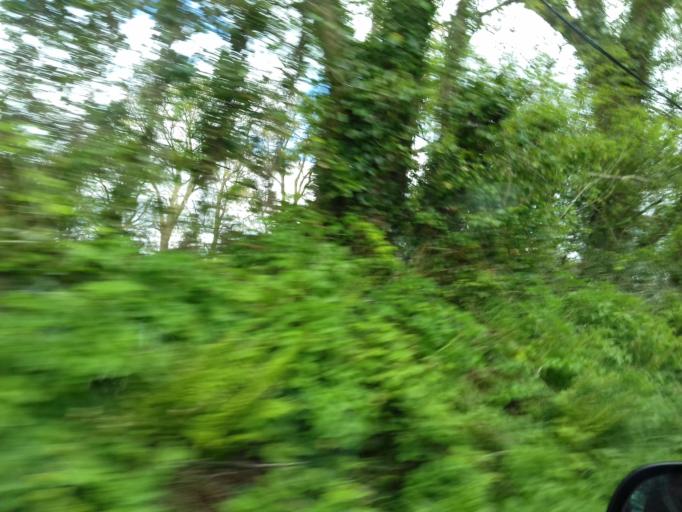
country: IE
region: Leinster
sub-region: Loch Garman
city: Castlebridge
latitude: 52.3818
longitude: -6.5019
